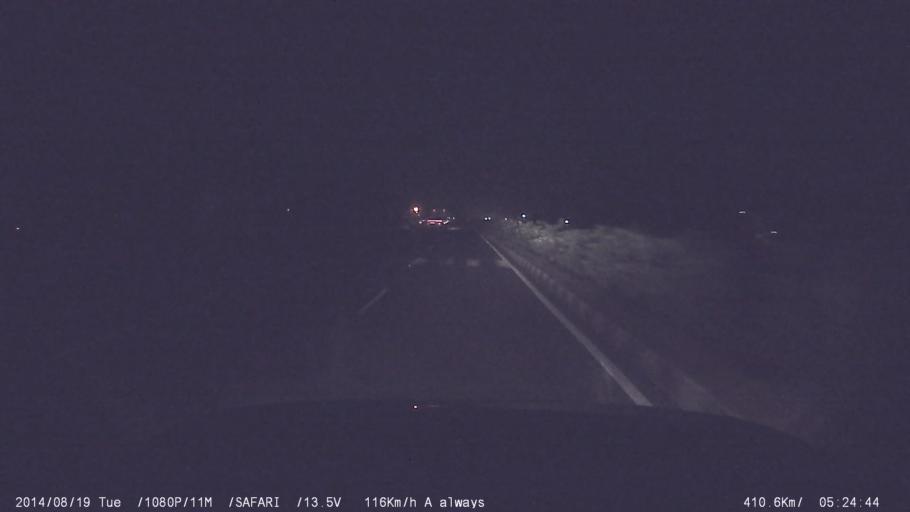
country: IN
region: Tamil Nadu
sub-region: Salem
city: Attayyampatti
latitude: 11.5687
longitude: 78.0321
